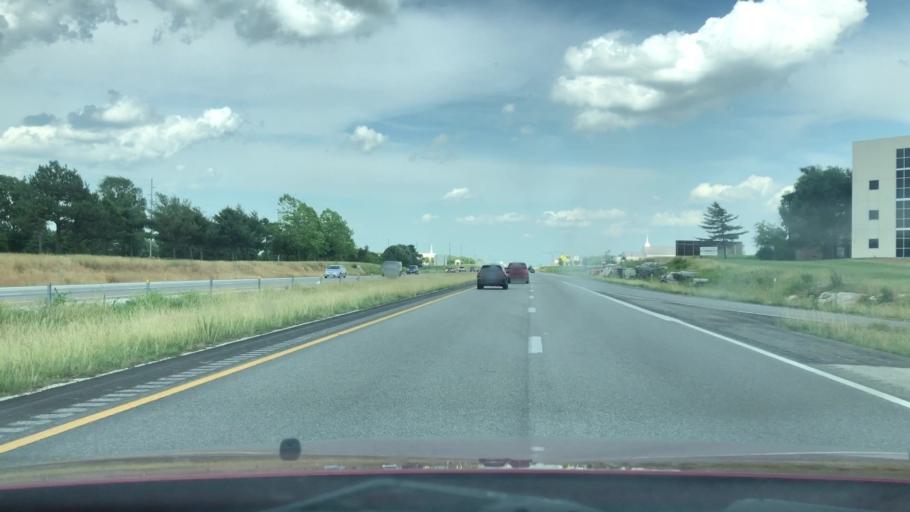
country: US
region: Missouri
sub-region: Greene County
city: Springfield
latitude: 37.2502
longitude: -93.2587
